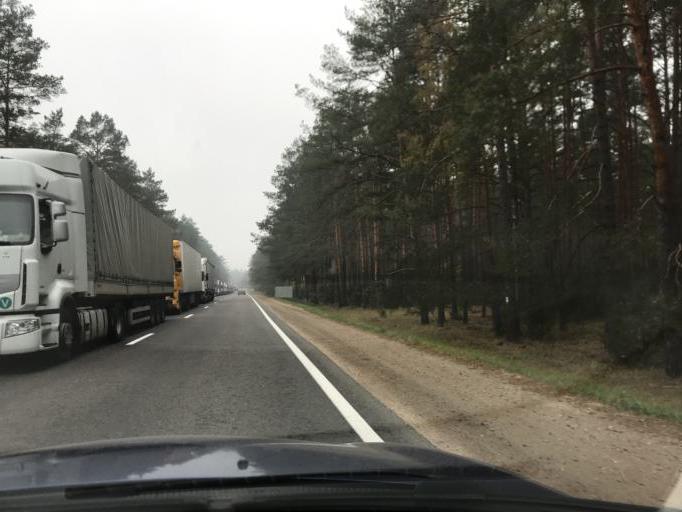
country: LT
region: Alytaus apskritis
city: Druskininkai
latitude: 53.9339
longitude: 23.9471
